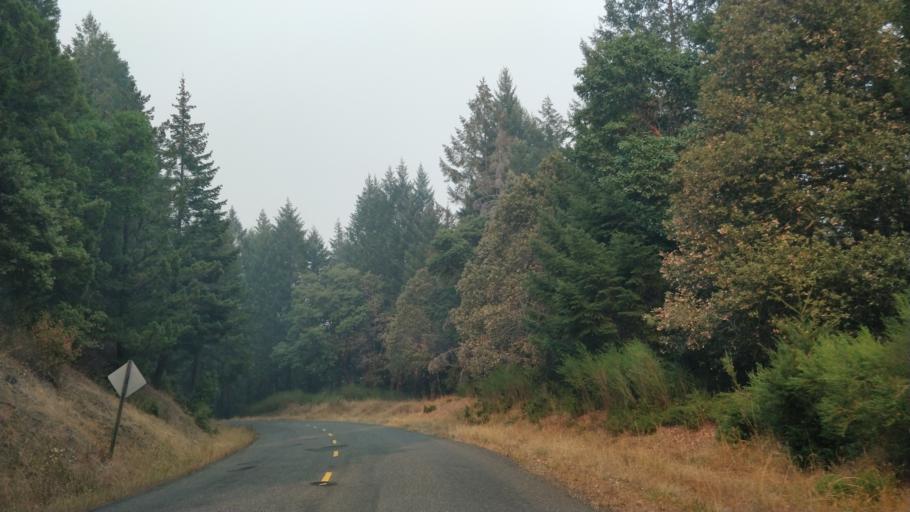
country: US
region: California
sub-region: Humboldt County
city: Rio Dell
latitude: 40.3258
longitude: -124.0422
